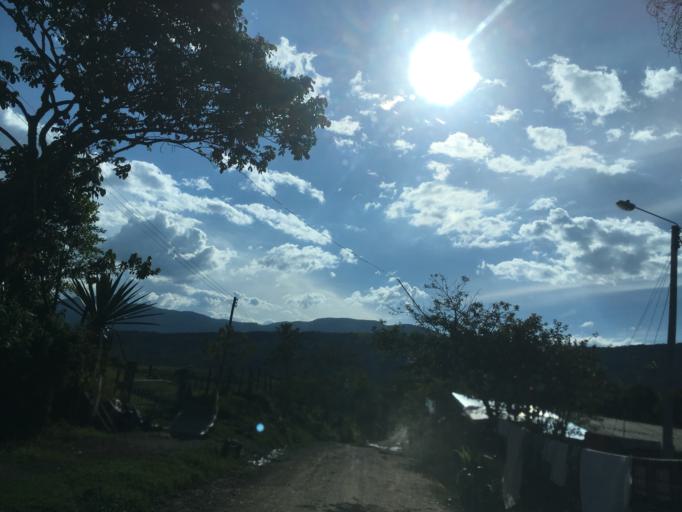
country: CO
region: Santander
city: Oiba
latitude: 6.1168
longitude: -73.1942
